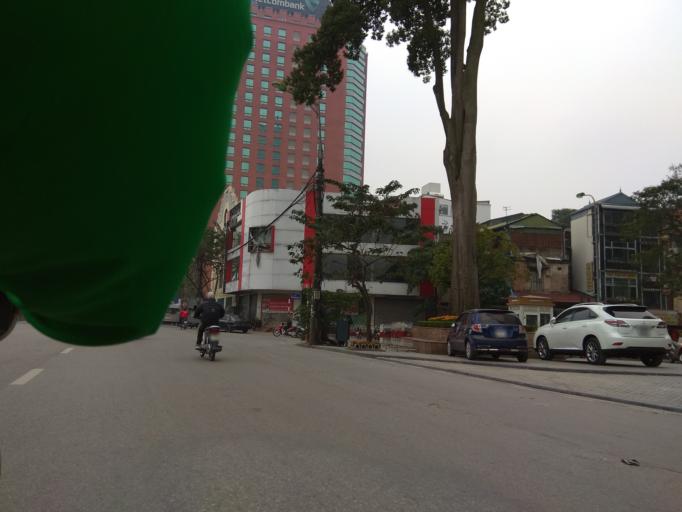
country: VN
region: Ha Noi
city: Hoan Kiem
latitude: 21.0293
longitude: 105.8573
